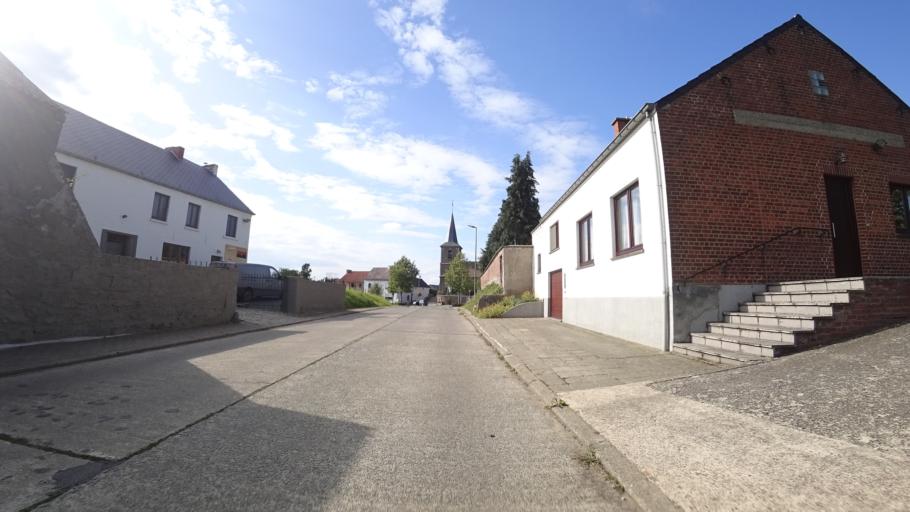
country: BE
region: Wallonia
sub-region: Province du Brabant Wallon
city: Chastre
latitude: 50.5797
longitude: 4.6129
